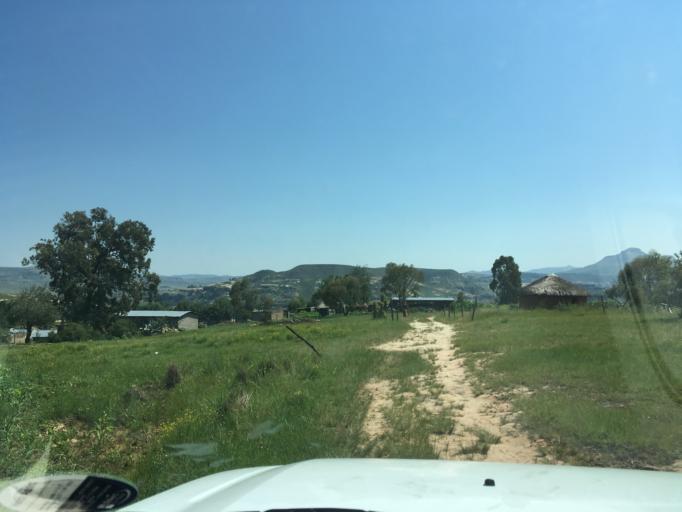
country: LS
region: Butha-Buthe
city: Butha-Buthe
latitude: -28.7247
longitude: 28.3667
